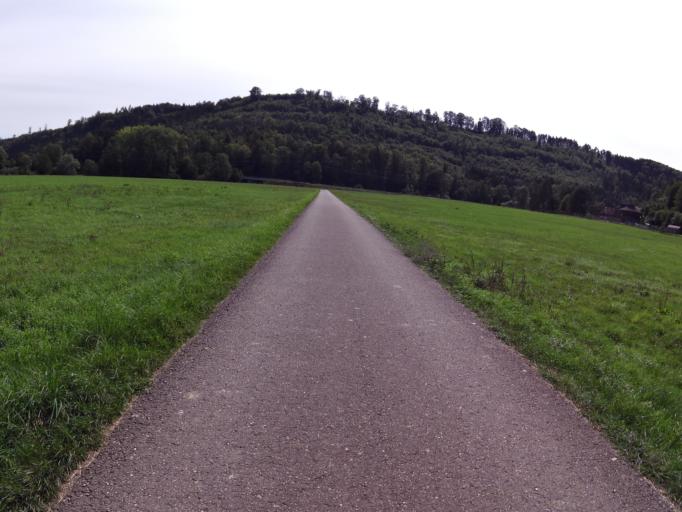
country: DE
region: Baden-Wuerttemberg
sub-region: Freiburg Region
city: Sulz am Neckar
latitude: 48.3975
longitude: 8.6422
